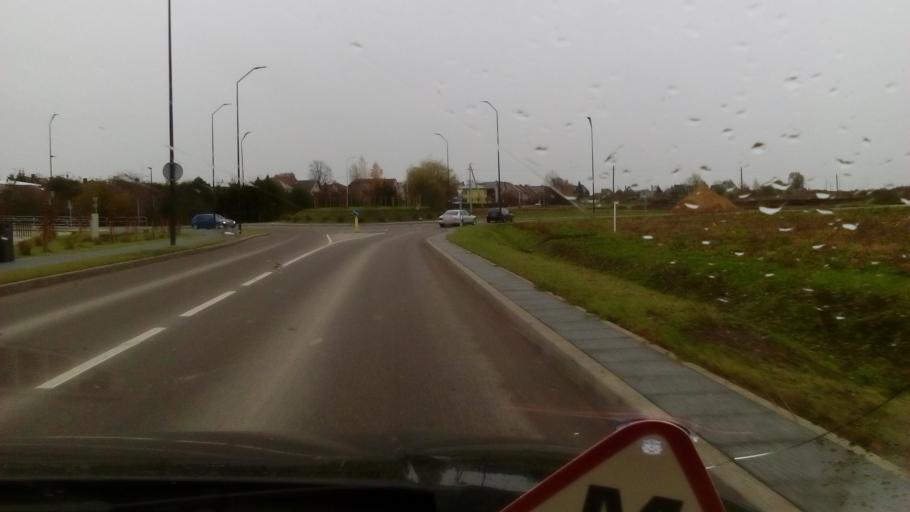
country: LT
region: Marijampoles apskritis
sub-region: Marijampole Municipality
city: Marijampole
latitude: 54.5439
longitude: 23.3570
